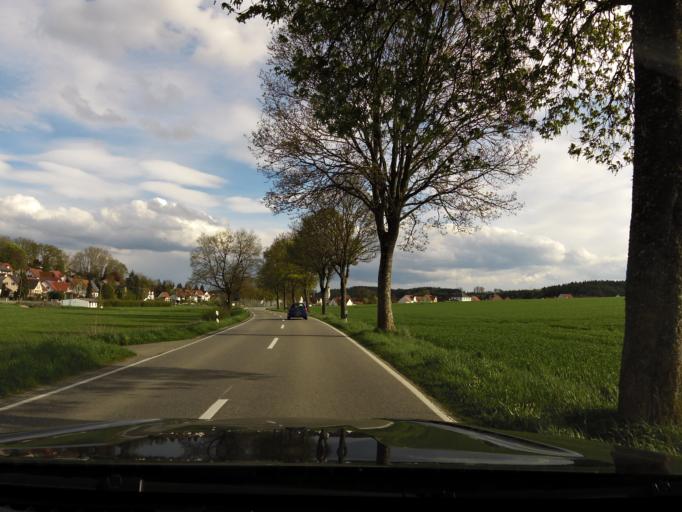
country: DE
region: Bavaria
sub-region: Upper Bavaria
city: Mauern
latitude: 48.5224
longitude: 11.8937
